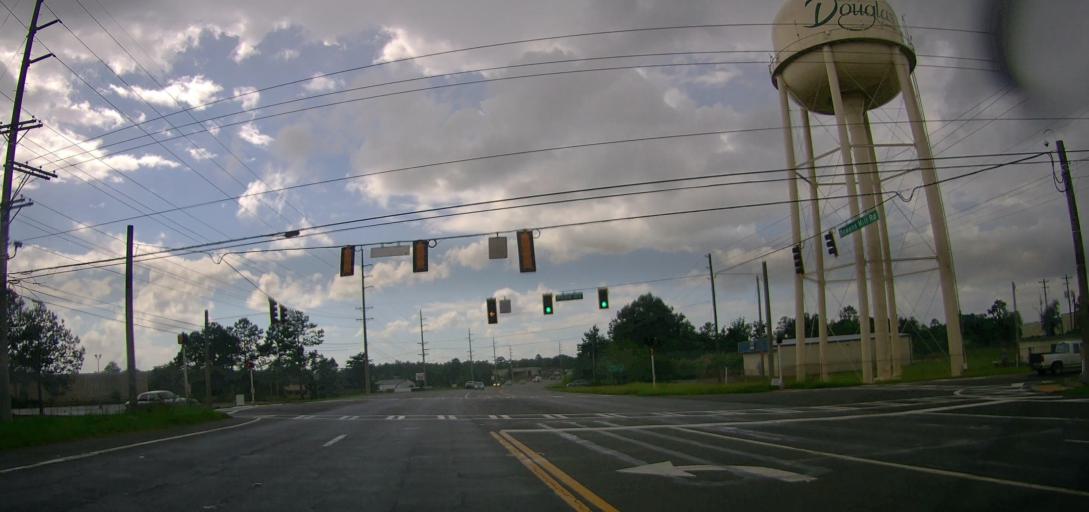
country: US
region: Georgia
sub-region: Coffee County
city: Douglas
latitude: 31.4889
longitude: -82.8666
